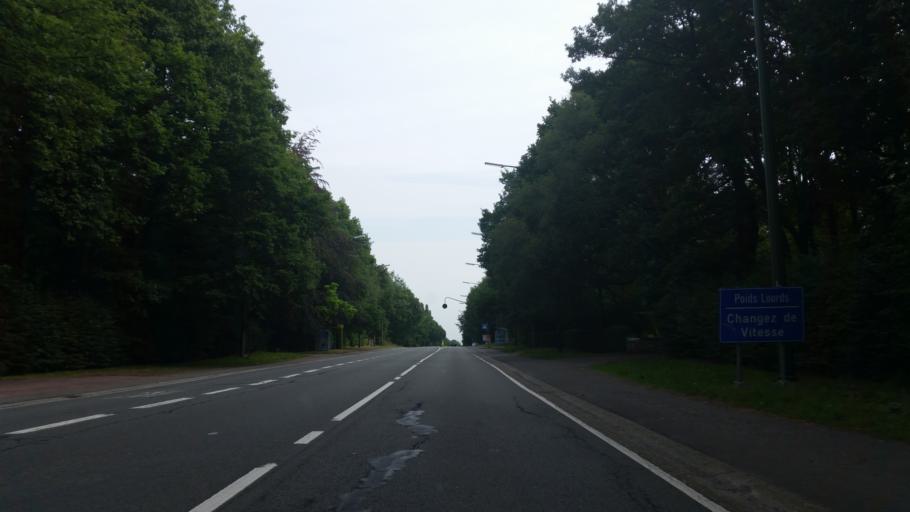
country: BE
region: Wallonia
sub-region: Province de Liege
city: Liege
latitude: 50.5940
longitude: 5.5735
